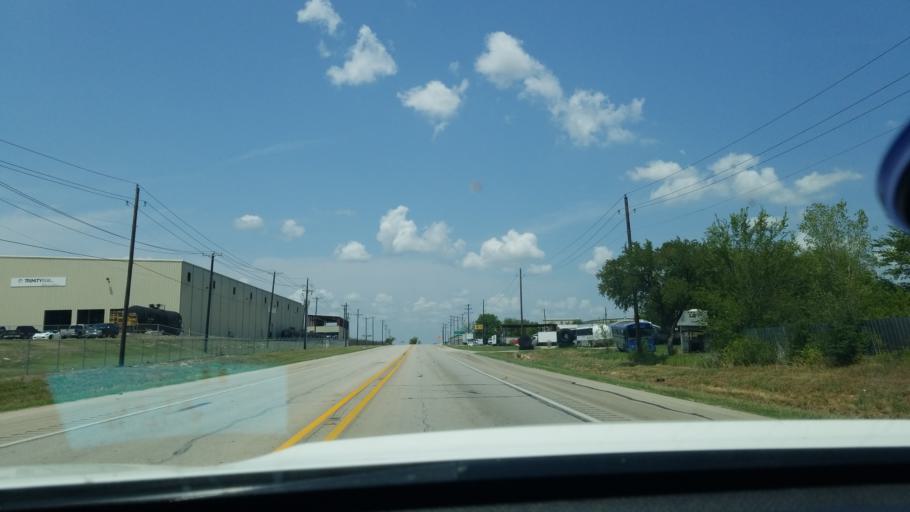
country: US
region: Texas
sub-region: Tarrant County
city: Eagle Mountain
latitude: 32.9362
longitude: -97.4182
